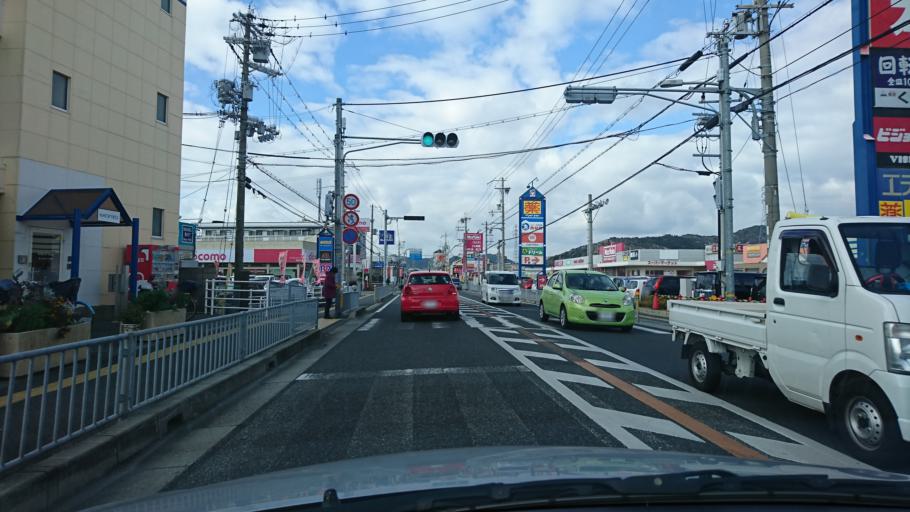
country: JP
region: Hyogo
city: Kakogawacho-honmachi
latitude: 34.7854
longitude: 134.8073
